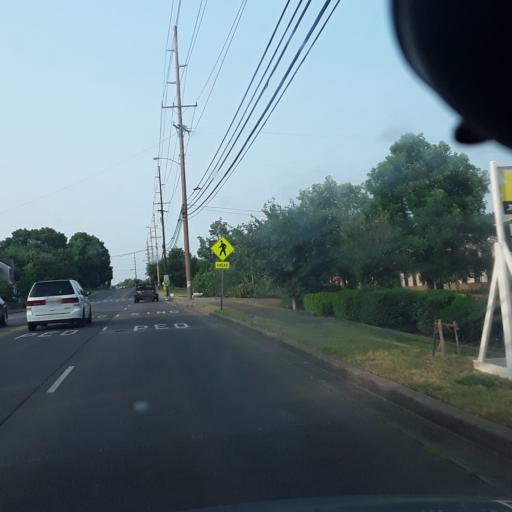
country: US
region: Tennessee
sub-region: Williamson County
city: Brentwood
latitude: 36.0463
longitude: -86.7440
